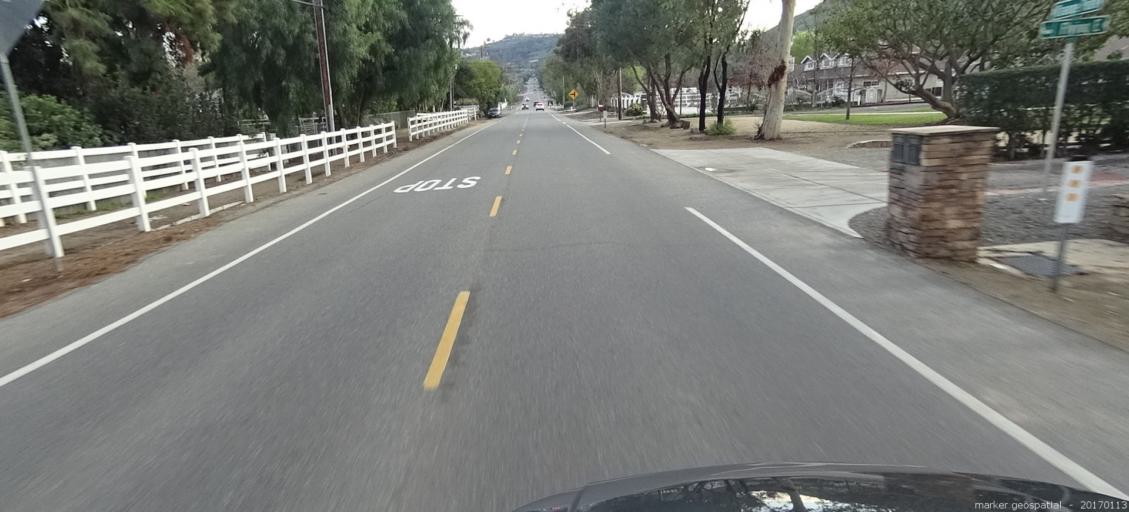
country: US
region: California
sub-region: Orange County
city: Villa Park
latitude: 33.8038
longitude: -117.7825
